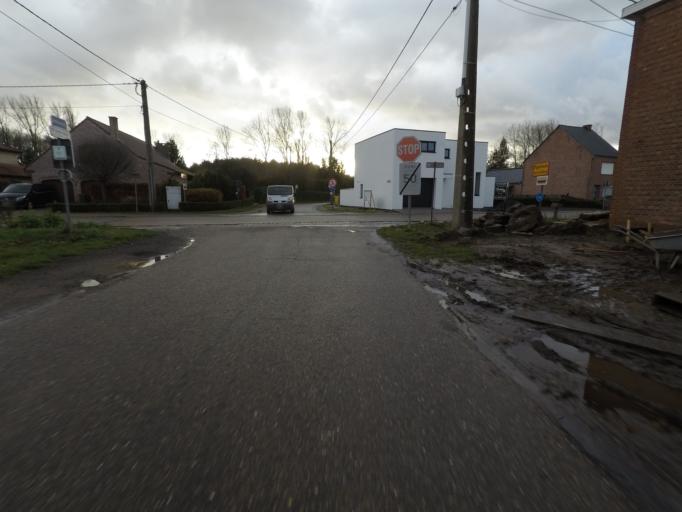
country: BE
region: Flanders
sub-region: Provincie Vlaams-Brabant
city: Begijnendijk
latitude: 51.0246
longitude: 4.7595
